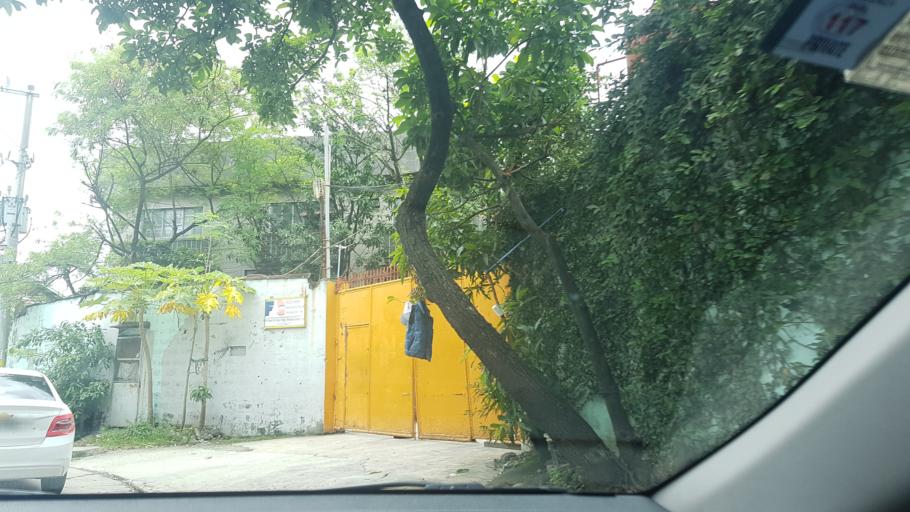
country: PH
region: Calabarzon
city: Del Monte
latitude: 14.6527
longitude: 121.0023
